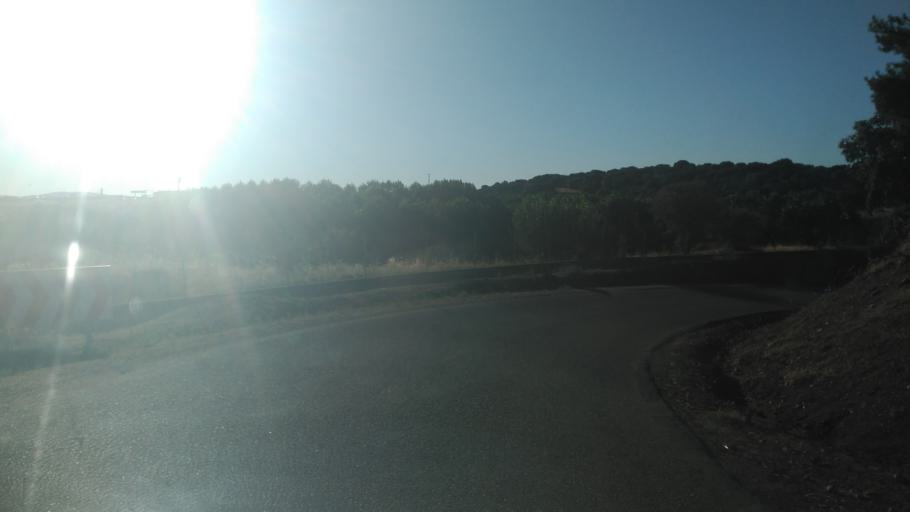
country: ES
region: Castille and Leon
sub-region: Provincia de Salamanca
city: Montejo
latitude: 40.6676
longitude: -5.6102
